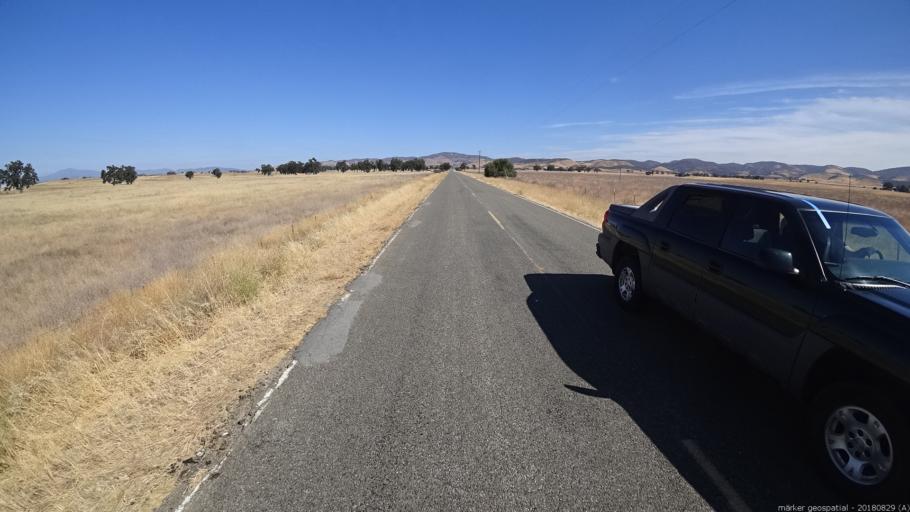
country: US
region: California
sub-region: San Luis Obispo County
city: Lake Nacimiento
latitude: 35.9294
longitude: -121.0822
